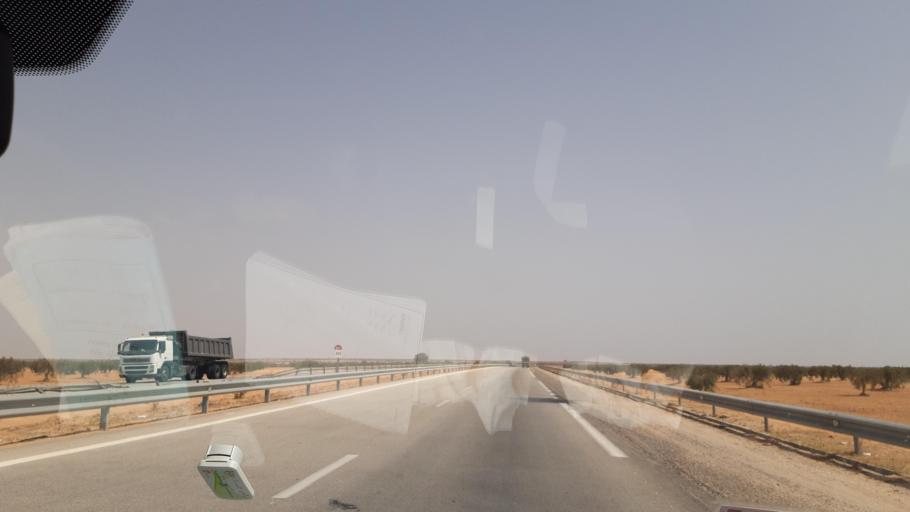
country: TN
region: Safaqis
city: Bi'r `Ali Bin Khalifah
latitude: 34.5279
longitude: 10.1226
